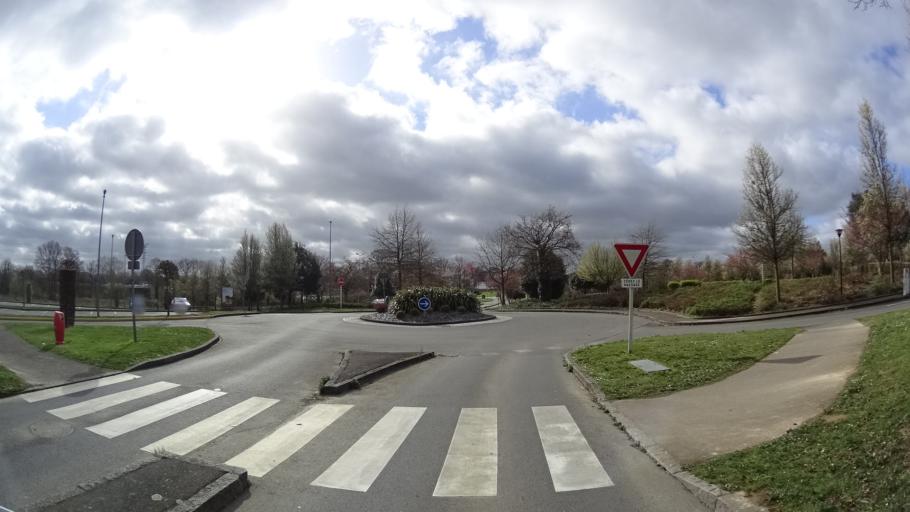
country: FR
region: Brittany
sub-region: Departement d'Ille-et-Vilaine
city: La Meziere
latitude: 48.2058
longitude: -1.7306
